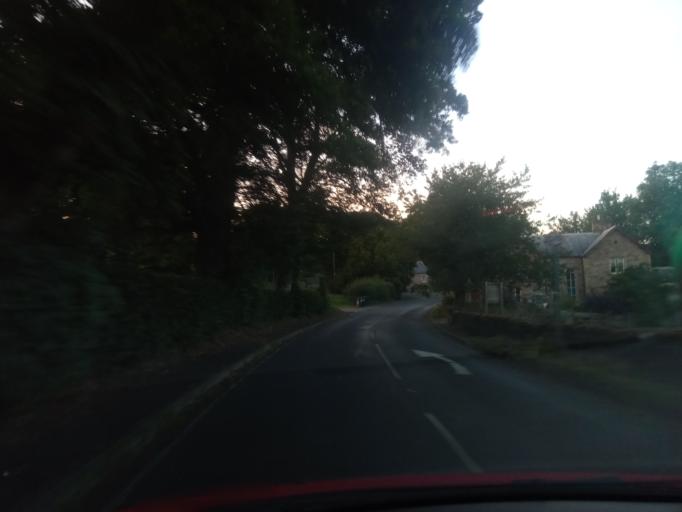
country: GB
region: England
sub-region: Northumberland
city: Bardon Mill
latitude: 54.9095
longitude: -2.3440
